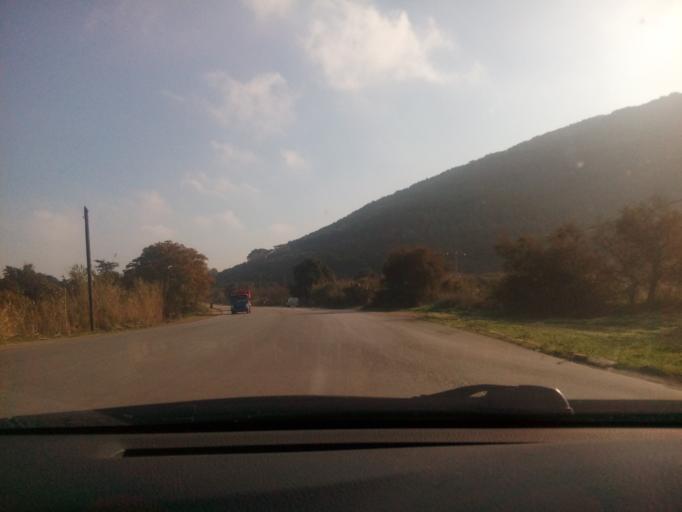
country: DZ
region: Oran
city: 'Ain el Turk
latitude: 35.7040
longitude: -0.8377
